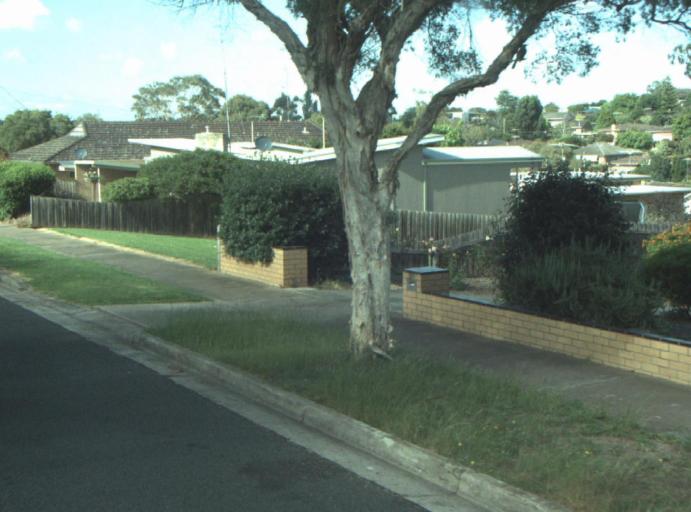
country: AU
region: Victoria
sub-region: Greater Geelong
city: Wandana Heights
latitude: -38.1769
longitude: 144.3251
